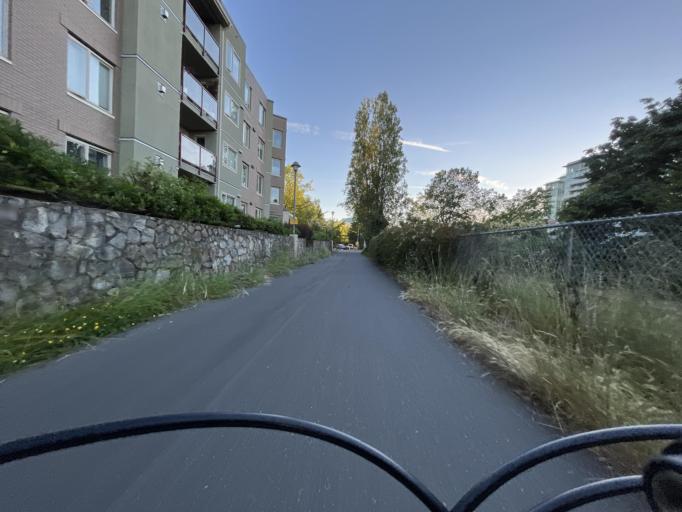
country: CA
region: British Columbia
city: Victoria
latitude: 48.4276
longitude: -123.3767
